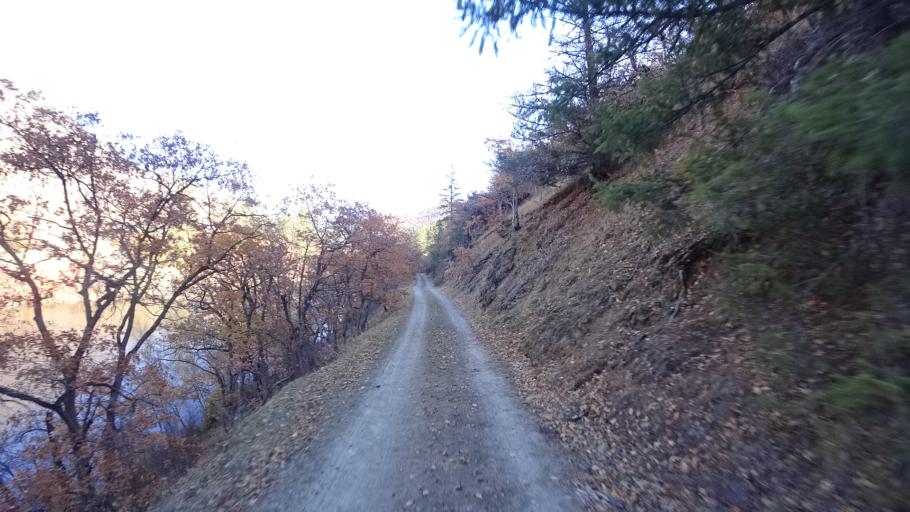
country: US
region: California
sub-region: Siskiyou County
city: Yreka
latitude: 41.8558
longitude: -122.7581
